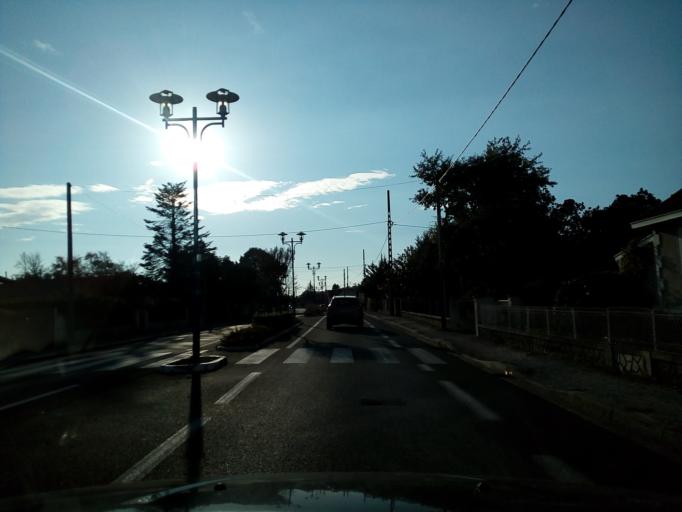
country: FR
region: Aquitaine
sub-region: Departement de la Gironde
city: Andernos-les-Bains
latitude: 44.7467
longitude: -1.0907
